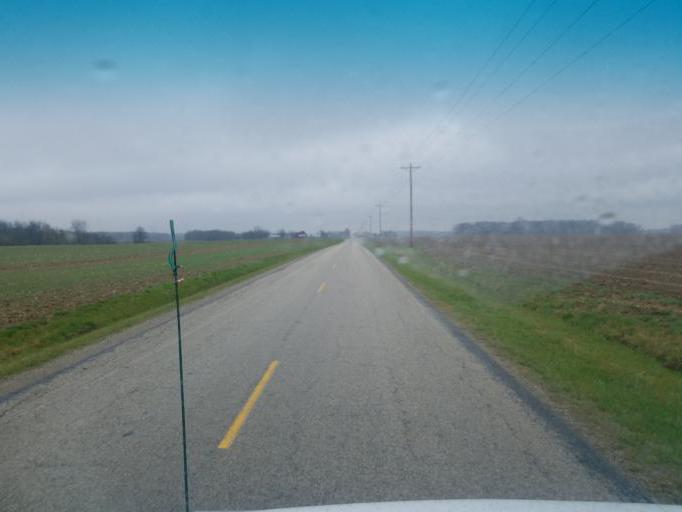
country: US
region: Ohio
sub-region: Crawford County
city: Bucyrus
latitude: 40.9648
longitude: -82.9770
